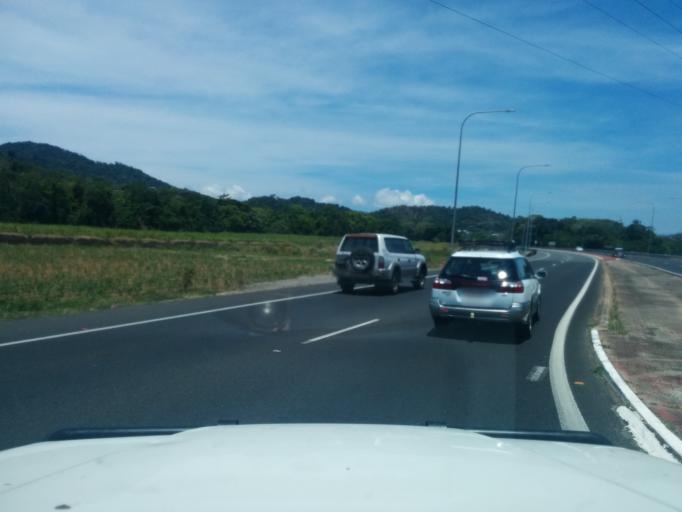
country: AU
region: Queensland
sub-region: Cairns
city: Redlynch
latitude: -16.8913
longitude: 145.7018
